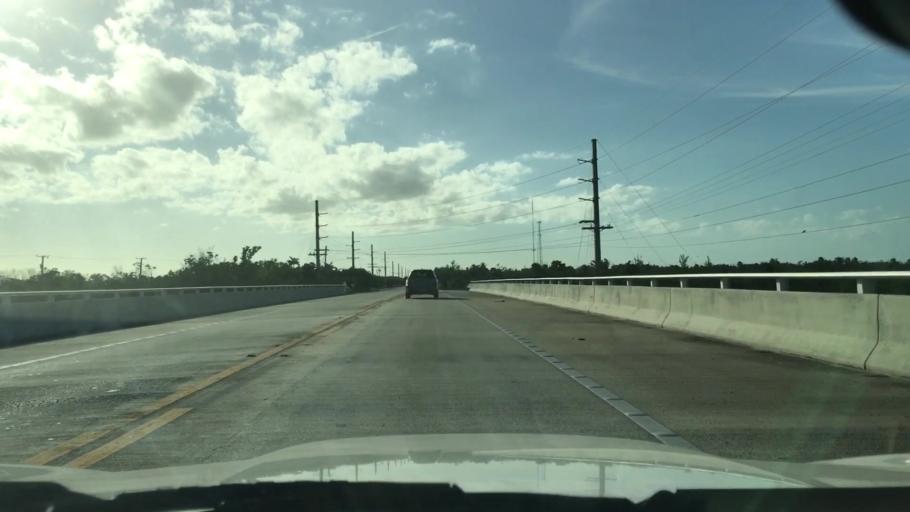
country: US
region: Florida
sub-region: Monroe County
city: Big Pine Key
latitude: 24.6631
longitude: -81.4028
